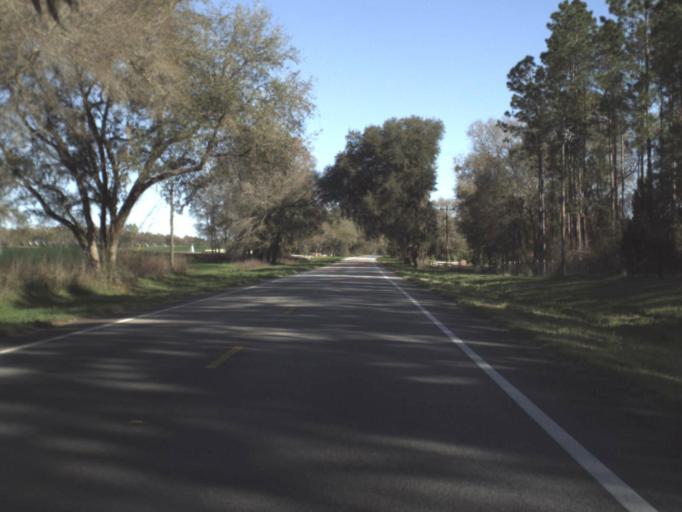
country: US
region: Georgia
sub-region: Brooks County
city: Quitman
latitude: 30.6037
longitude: -83.6448
